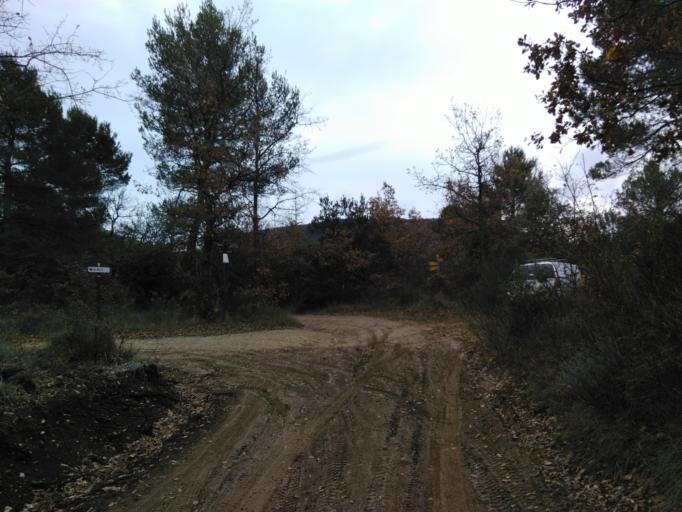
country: FR
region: Provence-Alpes-Cote d'Azur
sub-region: Departement du Vaucluse
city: Sablet
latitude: 44.1901
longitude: 5.0391
